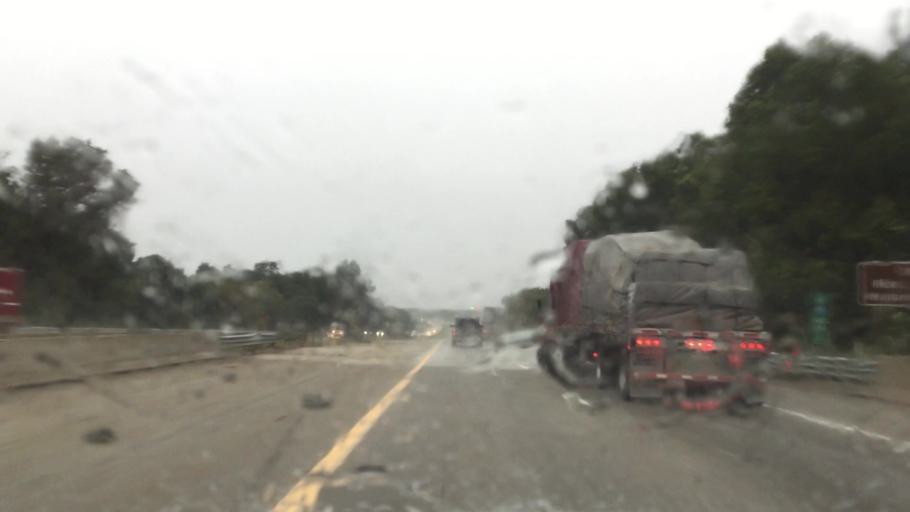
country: US
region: Michigan
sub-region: Van Buren County
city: Mattawan
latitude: 42.2232
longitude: -85.7669
